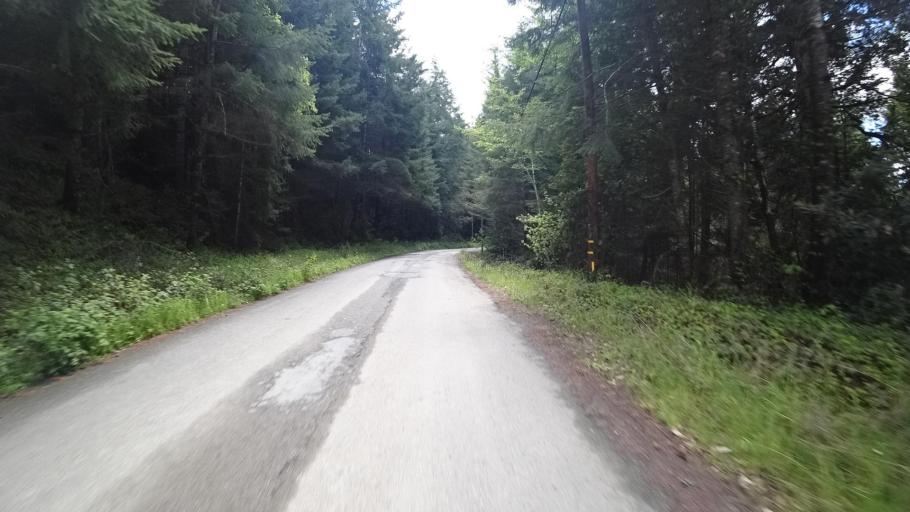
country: US
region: California
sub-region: Humboldt County
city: Blue Lake
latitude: 40.7905
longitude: -123.8810
